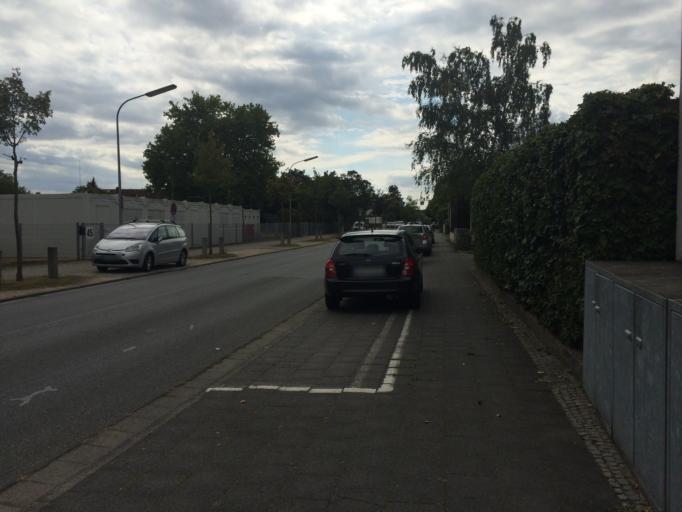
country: DE
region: Hesse
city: Morfelden-Walldorf
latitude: 50.0112
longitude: 8.5741
